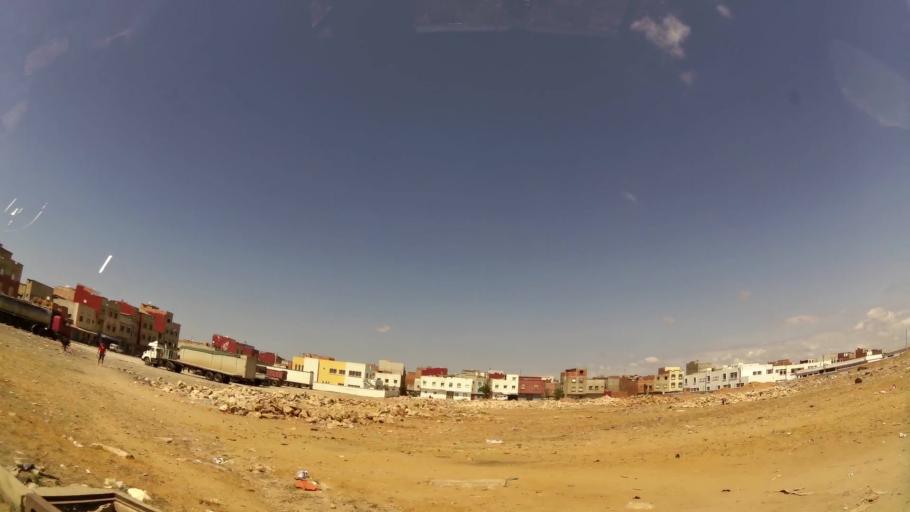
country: MA
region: Gharb-Chrarda-Beni Hssen
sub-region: Kenitra Province
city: Kenitra
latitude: 34.2279
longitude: -6.5493
